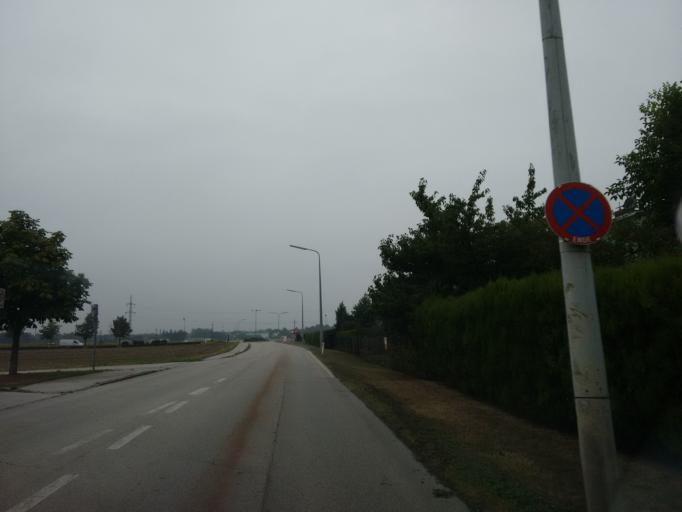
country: AT
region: Upper Austria
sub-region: Politischer Bezirk Linz-Land
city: Traun
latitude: 48.2205
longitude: 14.2215
